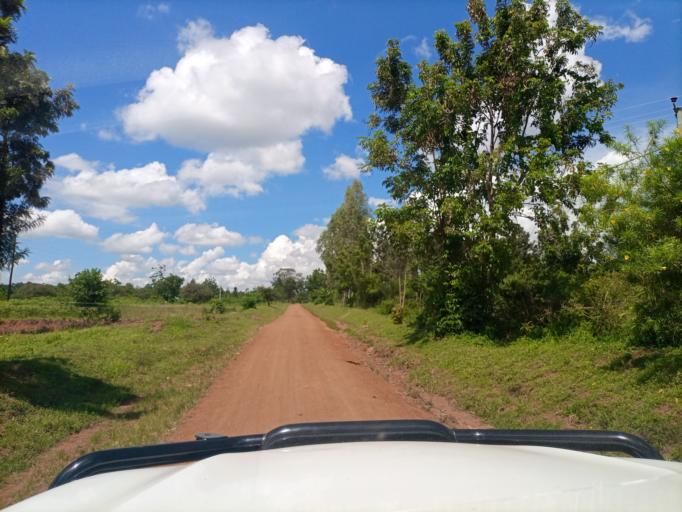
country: UG
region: Eastern Region
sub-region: Tororo District
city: Tororo
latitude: 0.7030
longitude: 34.0134
